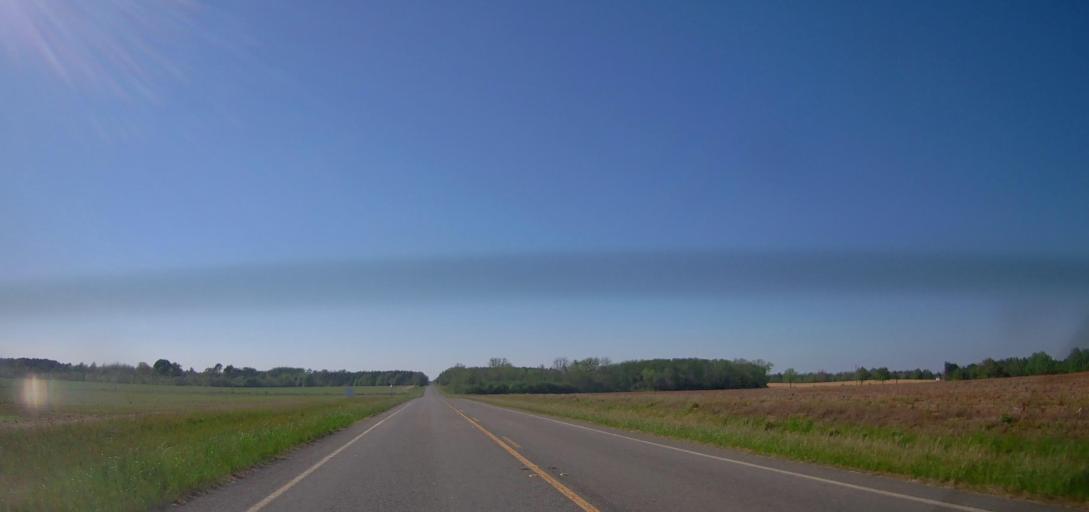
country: US
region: Georgia
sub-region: Wilcox County
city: Rochelle
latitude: 31.9901
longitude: -83.4668
